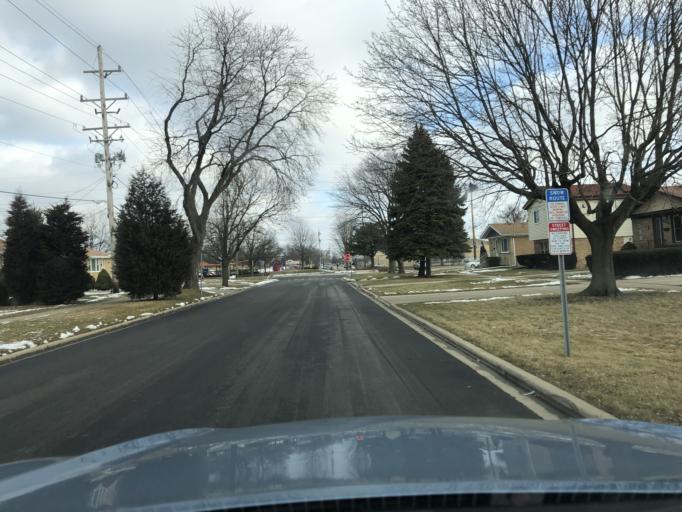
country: US
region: Illinois
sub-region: Cook County
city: Schiller Park
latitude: 41.9511
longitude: -87.8770
